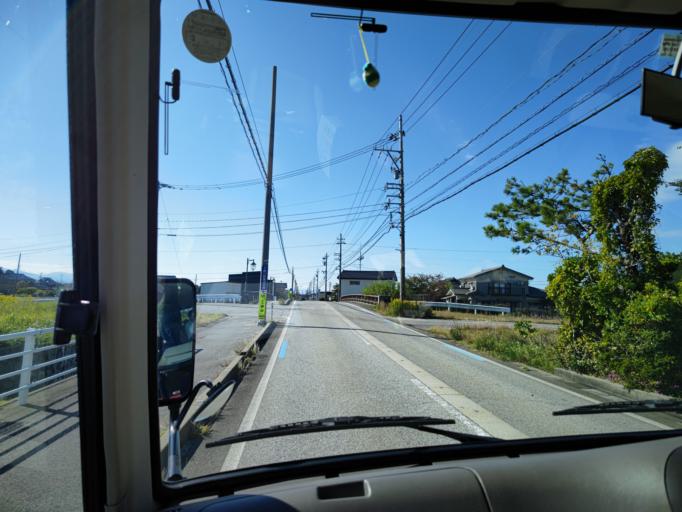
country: JP
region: Toyama
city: Nyuzen
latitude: 36.9034
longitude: 137.4238
